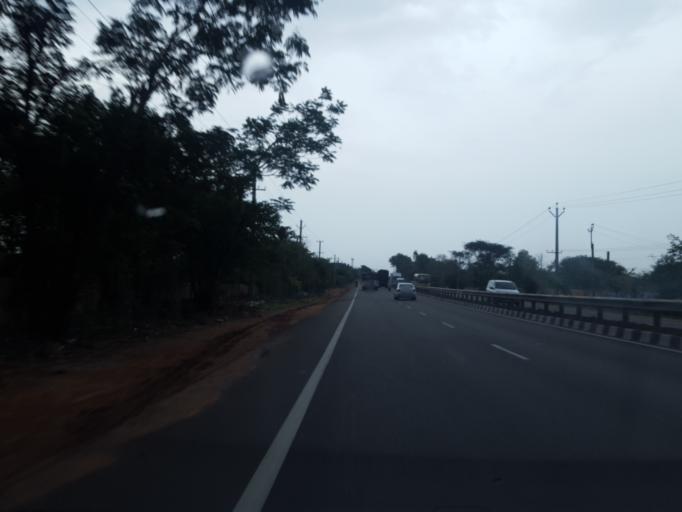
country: IN
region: Telangana
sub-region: Rangareddi
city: Sriramnagar
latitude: 17.1632
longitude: 78.2966
